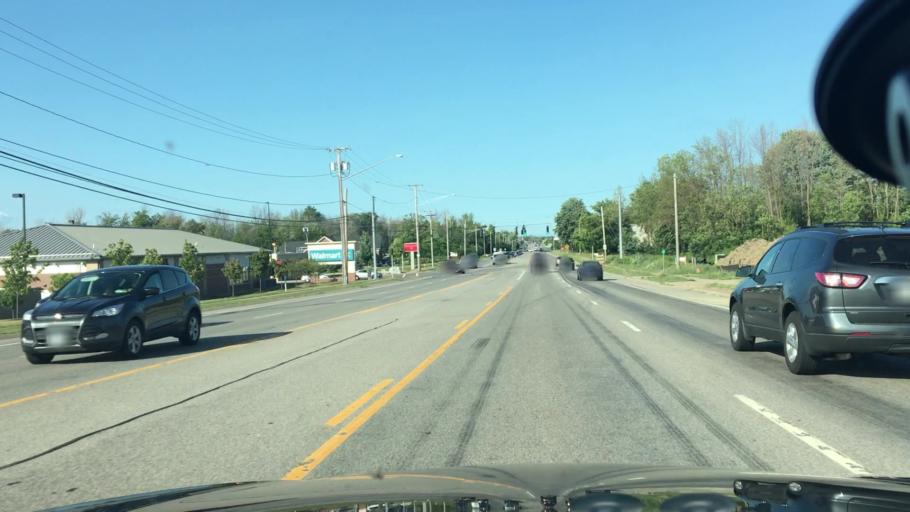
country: US
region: New York
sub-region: Erie County
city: Wanakah
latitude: 42.7410
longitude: -78.8705
